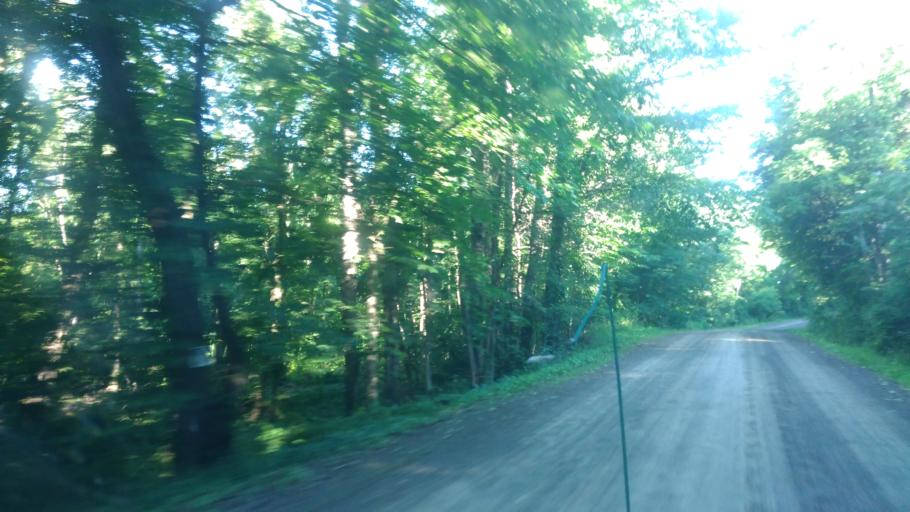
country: US
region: New York
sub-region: Wayne County
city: Sodus
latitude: 43.1635
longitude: -77.0580
